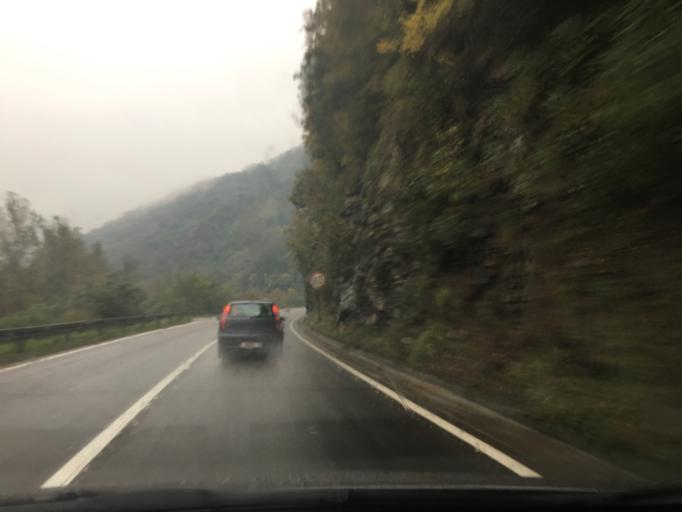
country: RS
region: Central Serbia
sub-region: Pcinjski Okrug
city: Vladicin Han
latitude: 42.7411
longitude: 22.0612
